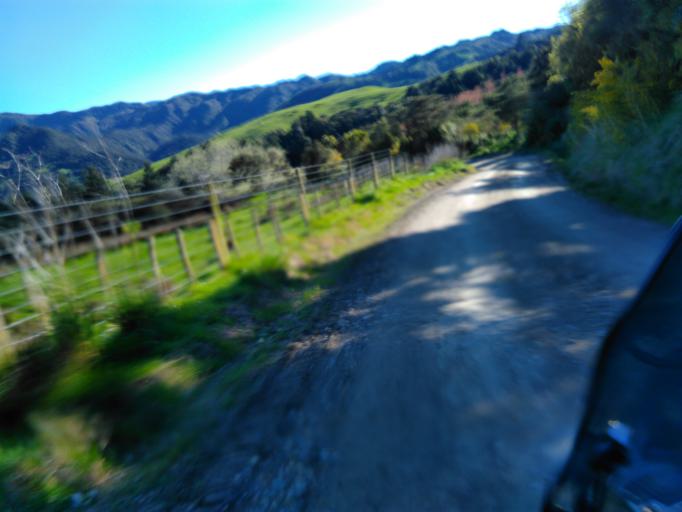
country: NZ
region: Gisborne
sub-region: Gisborne District
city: Gisborne
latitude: -38.3953
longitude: 177.6675
